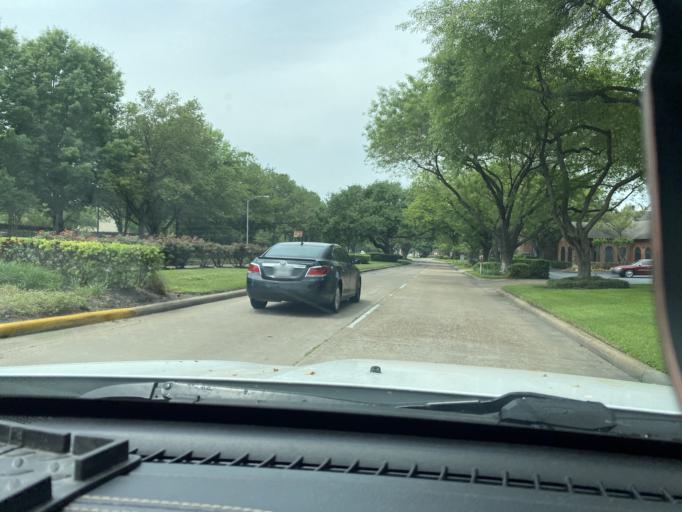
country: US
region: Texas
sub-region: Harris County
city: Jersey Village
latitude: 29.9099
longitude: -95.5803
